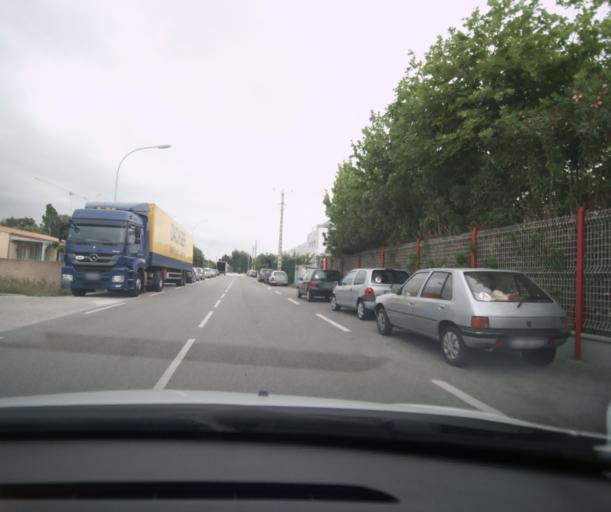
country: FR
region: Provence-Alpes-Cote d'Azur
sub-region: Departement du Var
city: La Farlede
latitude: 43.1408
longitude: 6.0327
